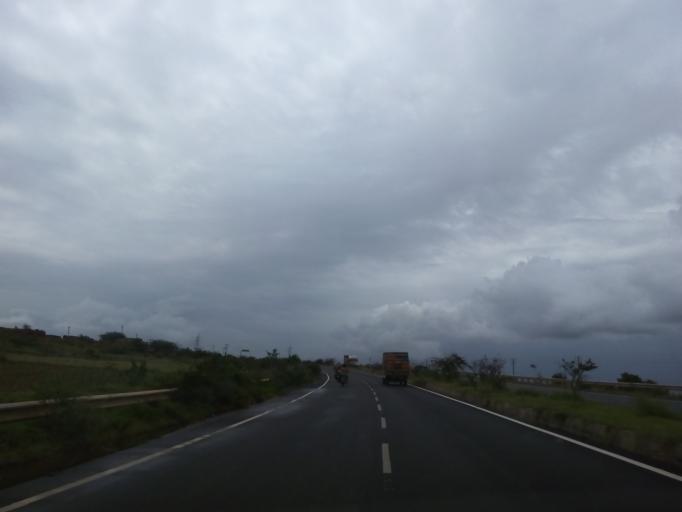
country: IN
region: Karnataka
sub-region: Haveri
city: Ranibennur
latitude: 14.5649
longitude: 75.7053
